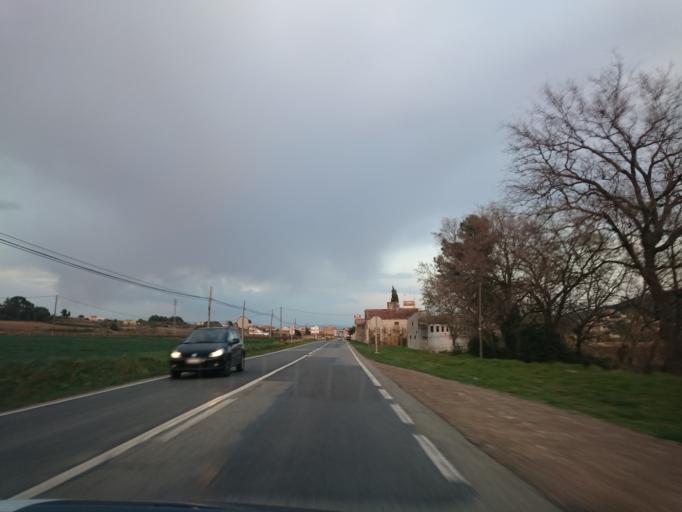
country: ES
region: Catalonia
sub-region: Provincia de Barcelona
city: Sant Marti Sarroca
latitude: 41.3896
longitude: 1.6001
